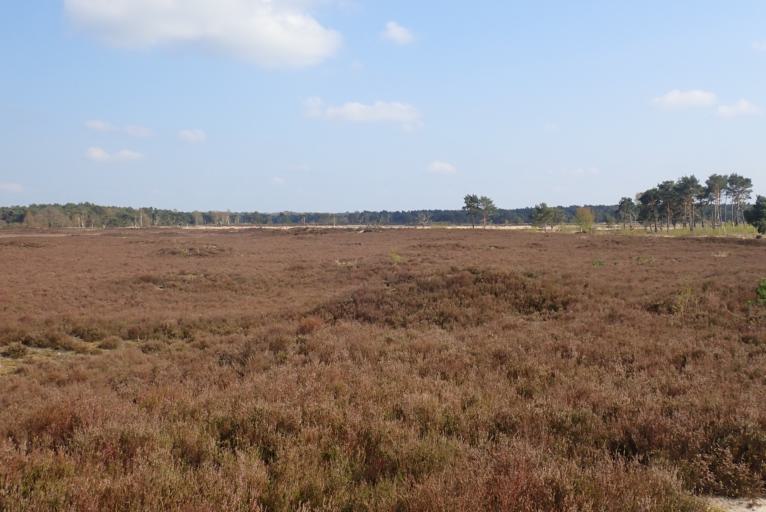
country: BE
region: Flanders
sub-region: Provincie Antwerpen
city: Kalmthout
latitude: 51.3857
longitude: 4.4304
